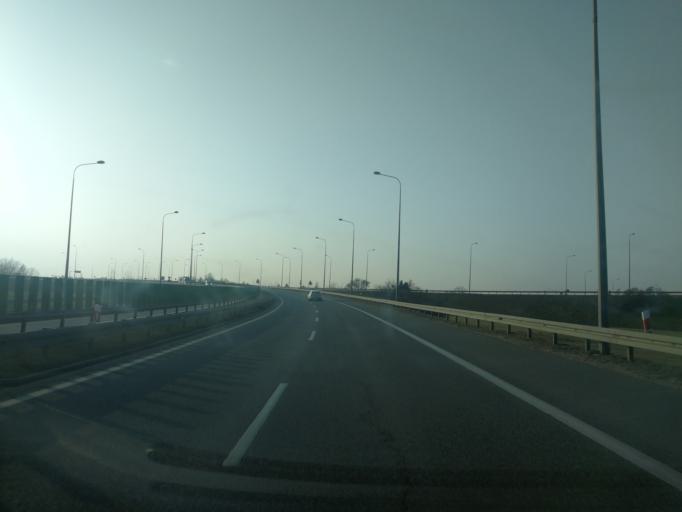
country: PL
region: Warmian-Masurian Voivodeship
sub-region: Powiat elblaski
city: Gronowo Gorne
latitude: 54.1375
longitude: 19.4498
